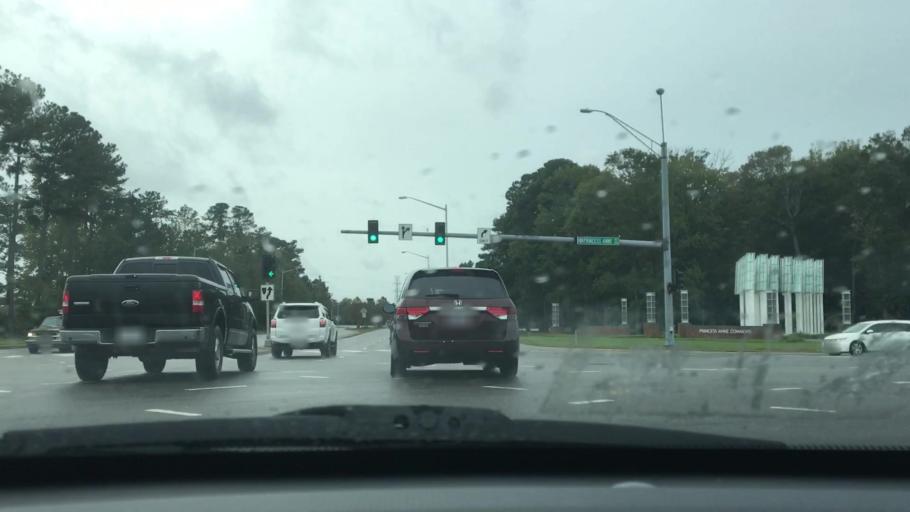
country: US
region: Virginia
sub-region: City of Virginia Beach
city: Virginia Beach
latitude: 36.7758
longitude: -76.0913
